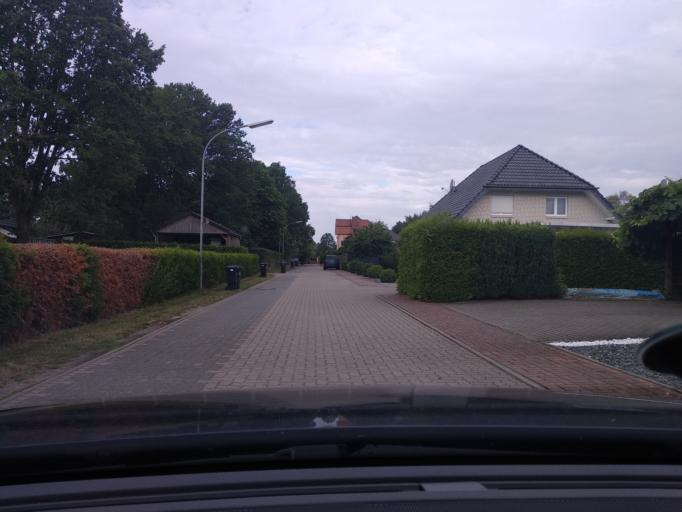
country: DE
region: Lower Saxony
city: Wagenhoff
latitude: 52.5126
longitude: 10.4808
